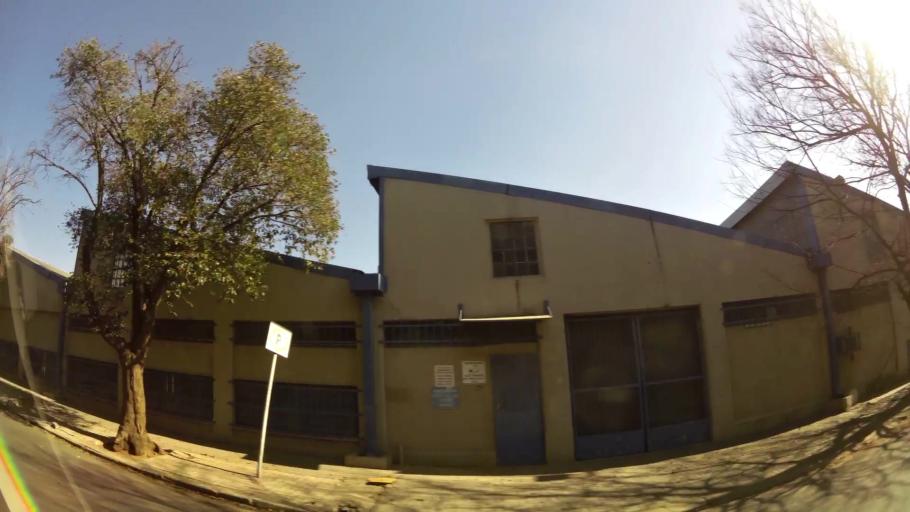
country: ZA
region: Gauteng
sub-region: City of Johannesburg Metropolitan Municipality
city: Johannesburg
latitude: -26.2020
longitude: 27.9797
